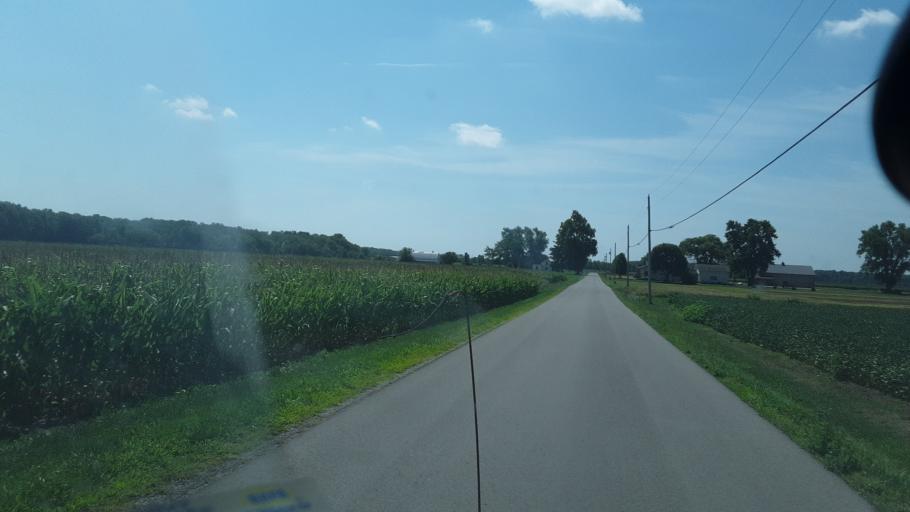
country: US
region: Ohio
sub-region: Wyandot County
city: Carey
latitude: 40.9976
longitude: -83.5162
